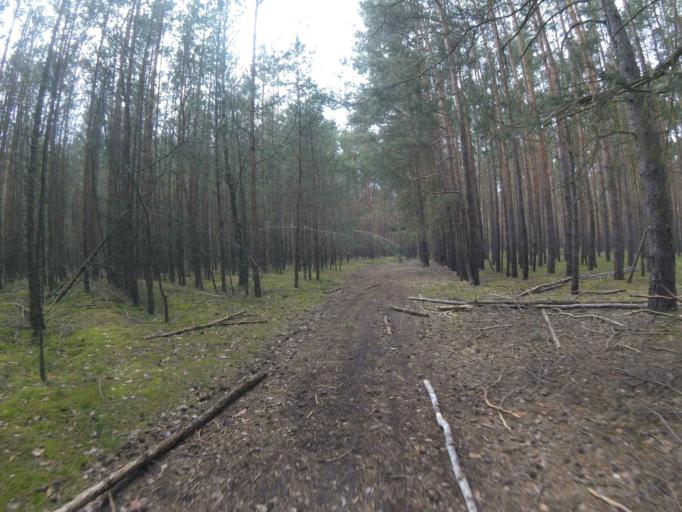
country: DE
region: Brandenburg
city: Bestensee
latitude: 52.2198
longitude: 13.6893
